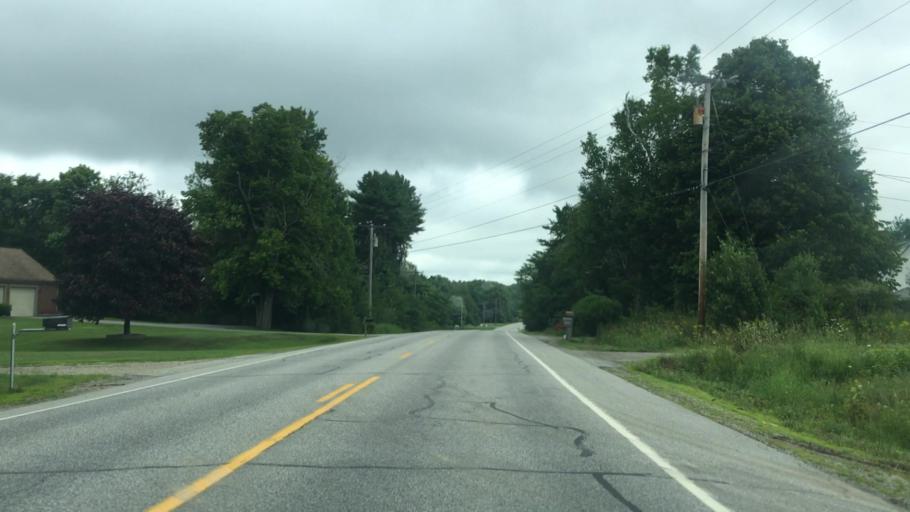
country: US
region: Maine
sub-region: Kennebec County
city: Pittston
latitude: 44.1606
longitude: -69.7450
